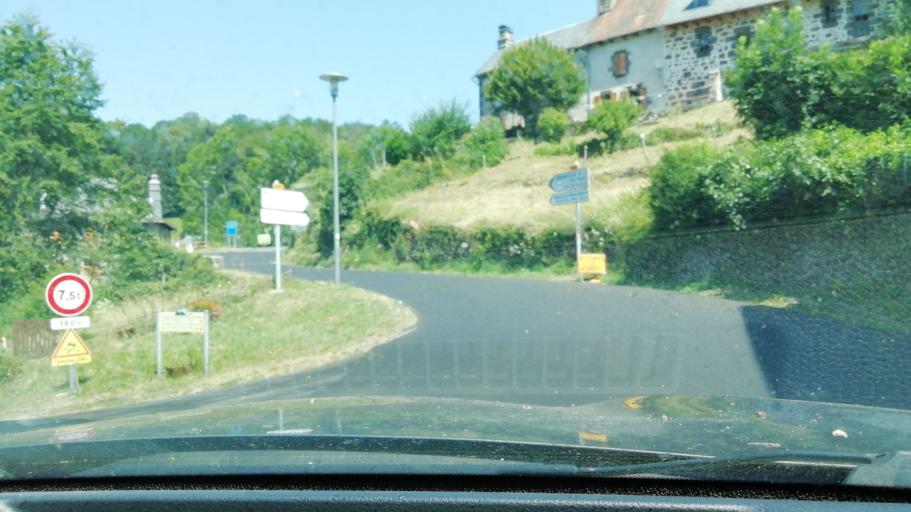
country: FR
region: Auvergne
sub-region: Departement du Cantal
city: Vic-sur-Cere
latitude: 45.0278
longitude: 2.5812
